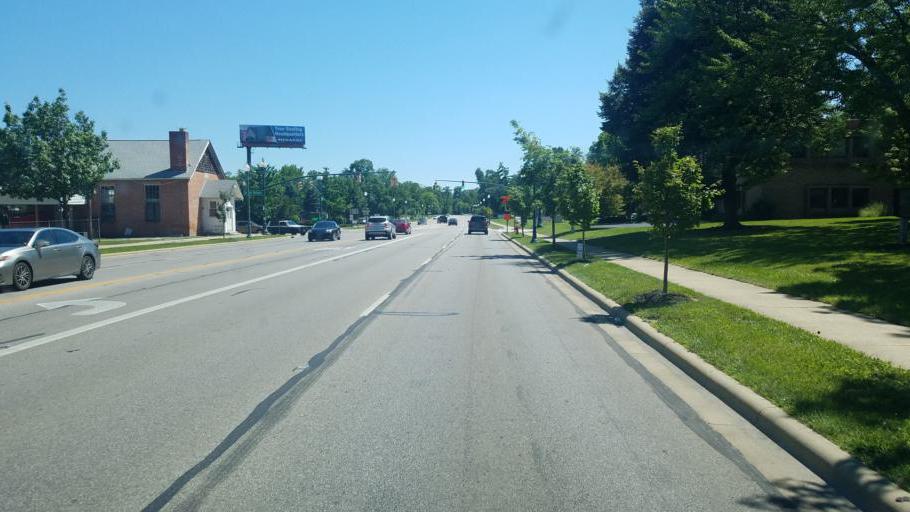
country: US
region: Ohio
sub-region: Franklin County
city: Huber Ridge
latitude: 40.1031
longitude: -82.8884
